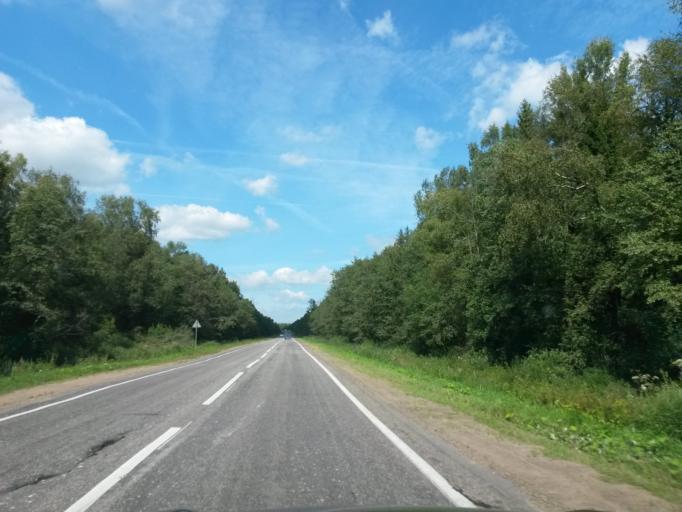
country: RU
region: Jaroslavl
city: Gavrilov-Yam
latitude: 57.4317
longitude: 39.9183
